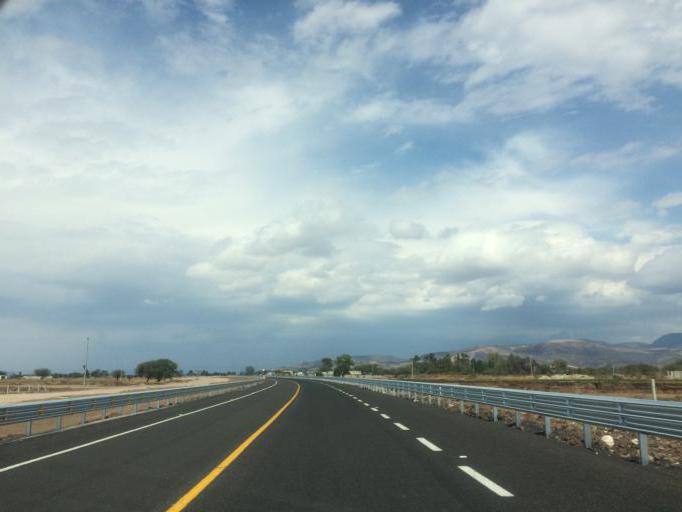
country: MX
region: Guanajuato
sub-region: Leon
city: Ladrilleras del Refugio
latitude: 21.0738
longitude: -101.5410
